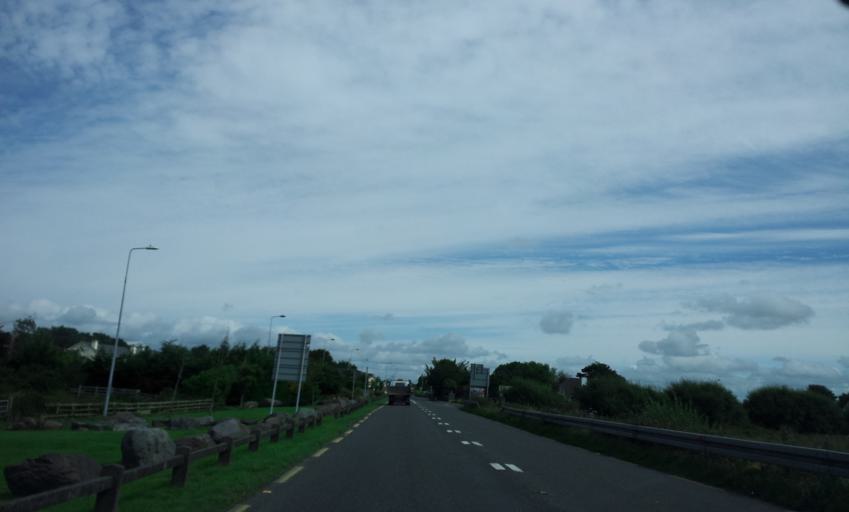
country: IE
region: Munster
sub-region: Ciarrai
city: Killorglin
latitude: 52.1034
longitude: -9.8043
